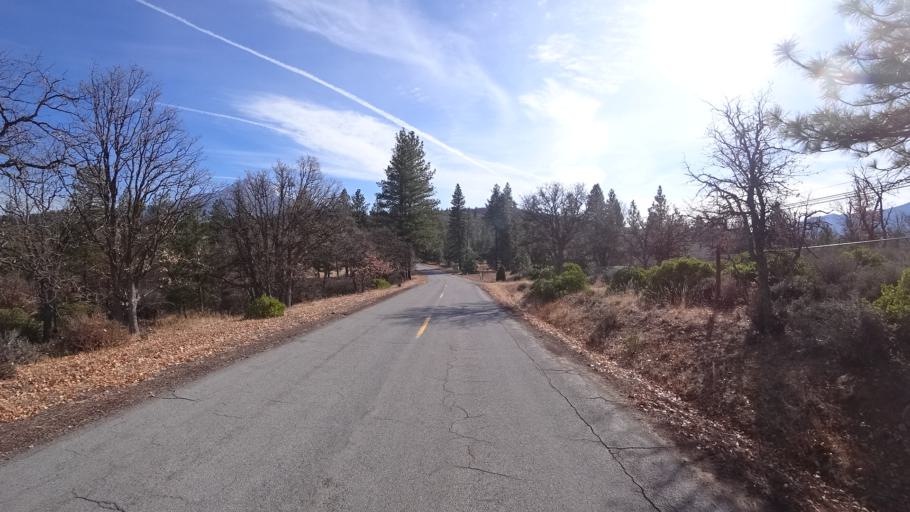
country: US
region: California
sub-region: Siskiyou County
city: Weed
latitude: 41.4308
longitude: -122.4247
